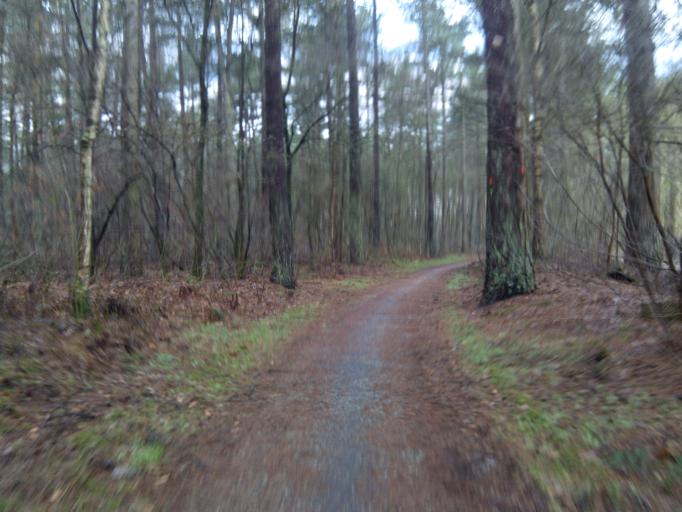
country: NL
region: Utrecht
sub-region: Gemeente Utrechtse Heuvelrug
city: Overberg
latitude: 52.0227
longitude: 5.4951
